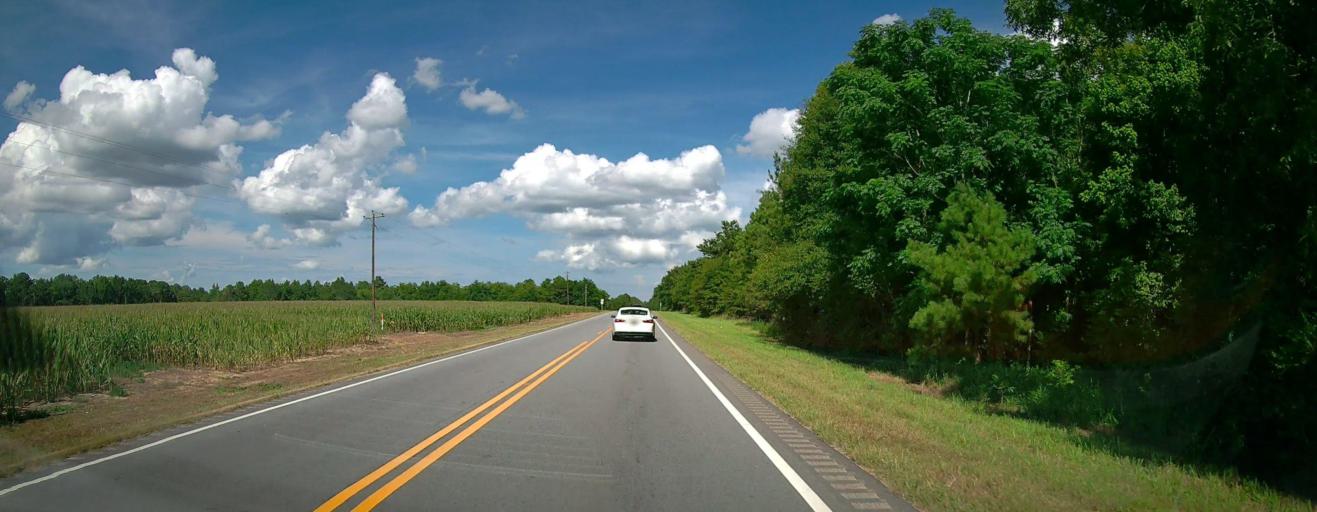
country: US
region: Alabama
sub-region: Lee County
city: Auburn
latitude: 32.4318
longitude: -85.4259
